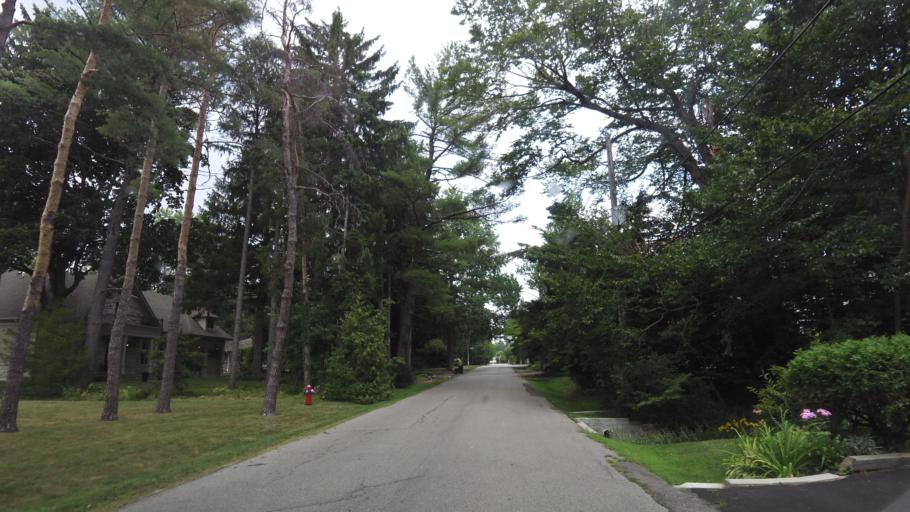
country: CA
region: Ontario
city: Mississauga
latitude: 43.5680
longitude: -79.5909
